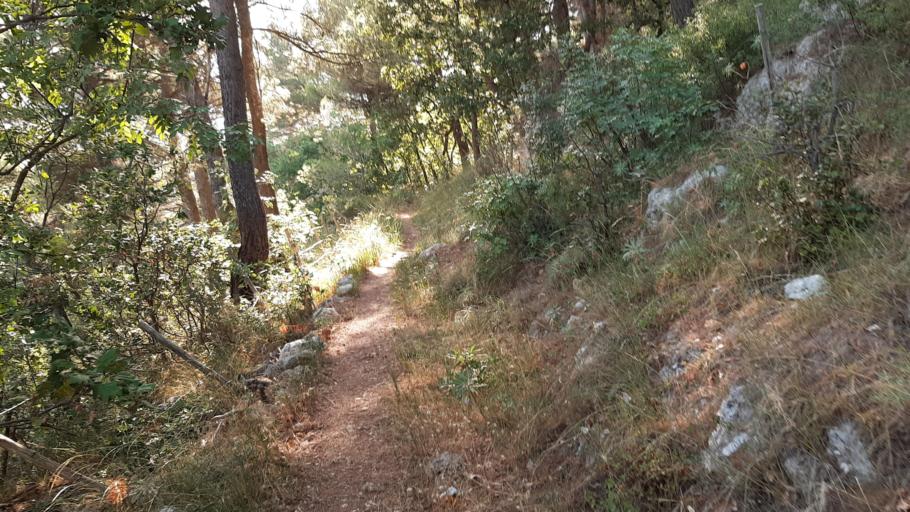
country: IT
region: Apulia
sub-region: Provincia di Foggia
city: San Giovanni Rotondo
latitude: 41.7106
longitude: 15.7150
